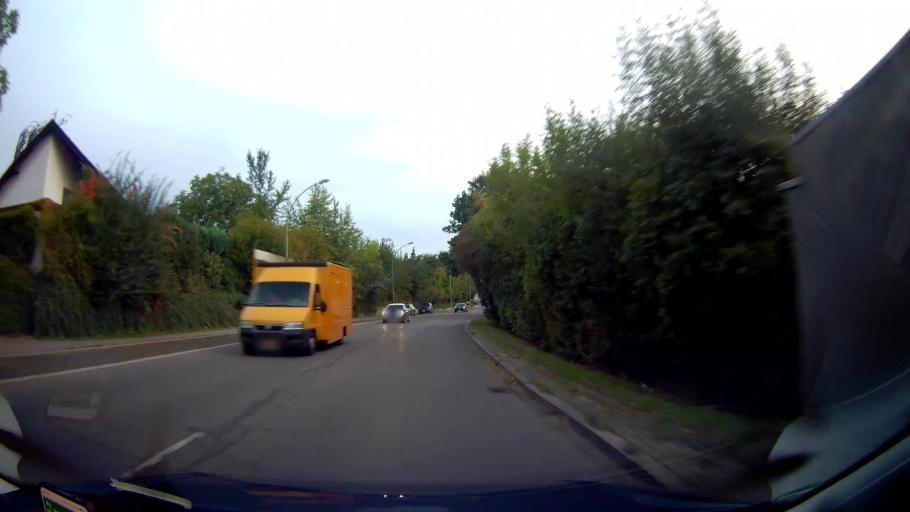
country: DE
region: North Rhine-Westphalia
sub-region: Regierungsbezirk Arnsberg
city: Herne
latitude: 51.5384
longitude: 7.2638
